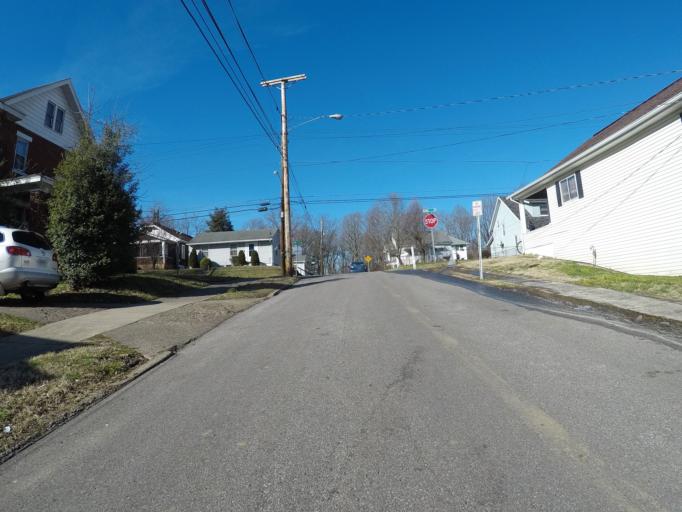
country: US
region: West Virginia
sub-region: Cabell County
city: Huntington
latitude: 38.4102
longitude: -82.4103
